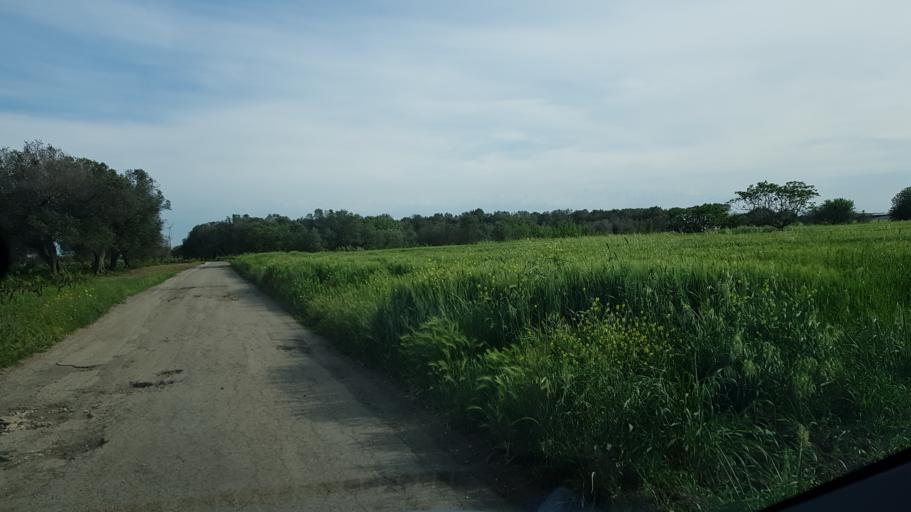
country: IT
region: Apulia
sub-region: Provincia di Brindisi
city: Tuturano
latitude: 40.5211
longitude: 17.9709
